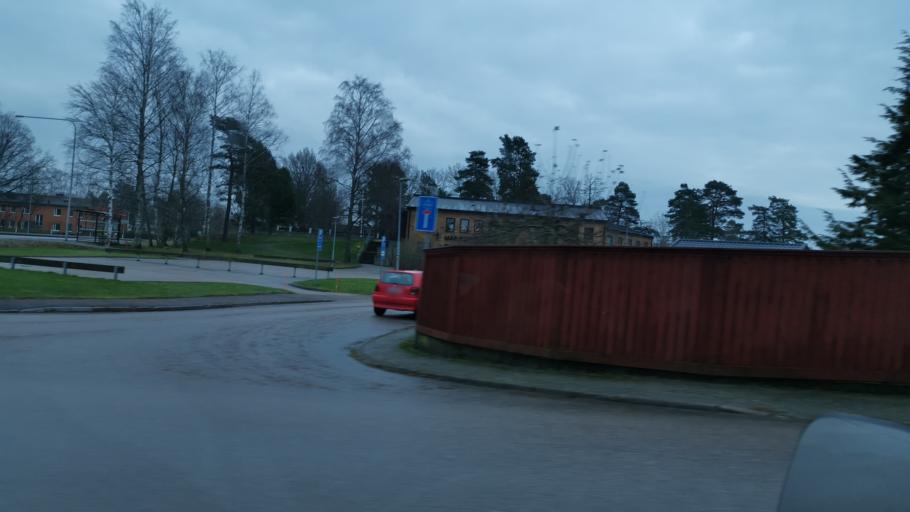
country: SE
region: Vaestra Goetaland
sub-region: Vanersborgs Kommun
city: Vanersborg
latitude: 58.3641
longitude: 12.3491
